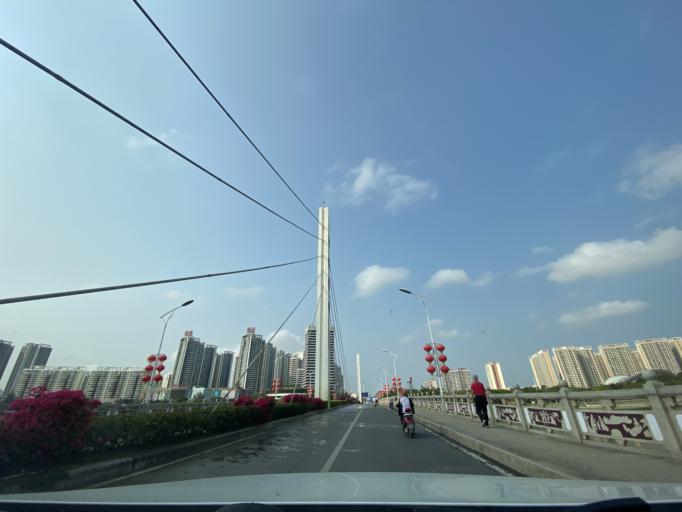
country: CN
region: Hainan
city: Yelin
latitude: 18.5173
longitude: 110.0313
